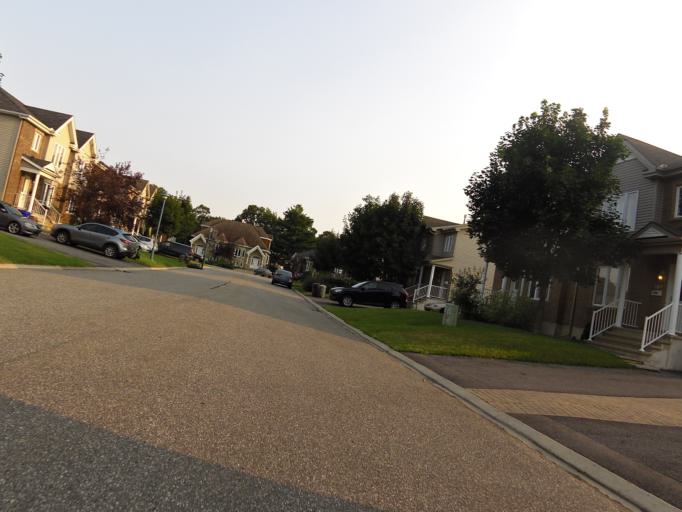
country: CA
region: Ontario
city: Bells Corners
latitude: 45.3827
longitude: -75.8290
